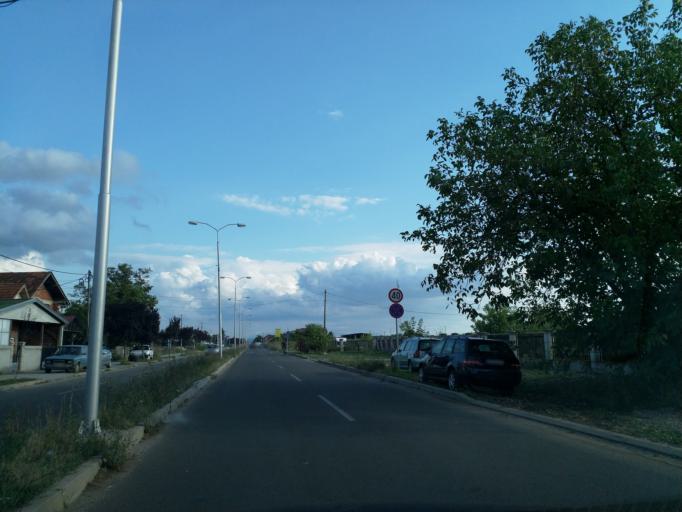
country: RS
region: Central Serbia
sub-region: Pomoravski Okrug
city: Paracin
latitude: 43.8465
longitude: 21.4141
